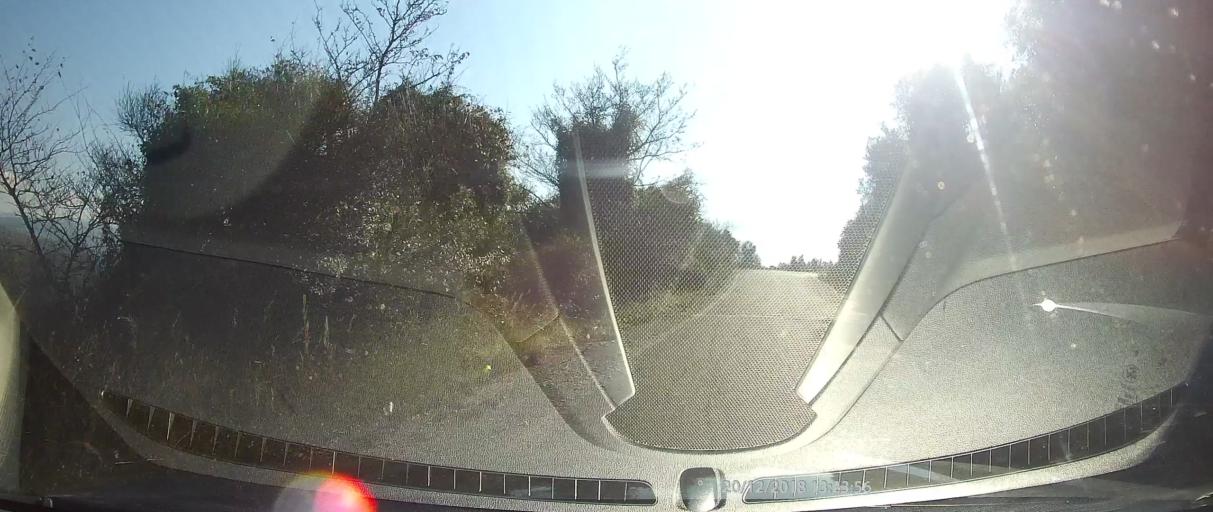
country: GR
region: West Greece
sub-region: Nomos Aitolias kai Akarnanias
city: Paravola
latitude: 38.6187
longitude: 21.5688
